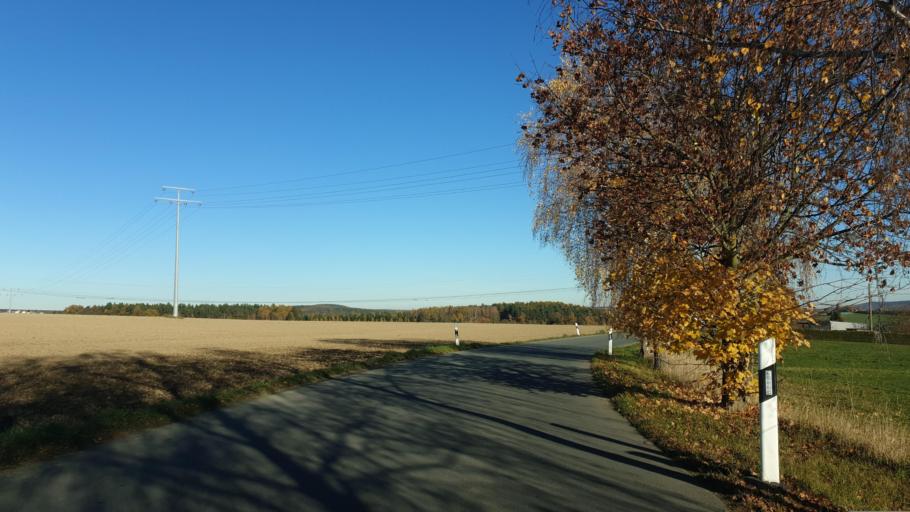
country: DE
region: Saxony
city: Elsterberg
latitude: 50.6427
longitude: 12.1515
